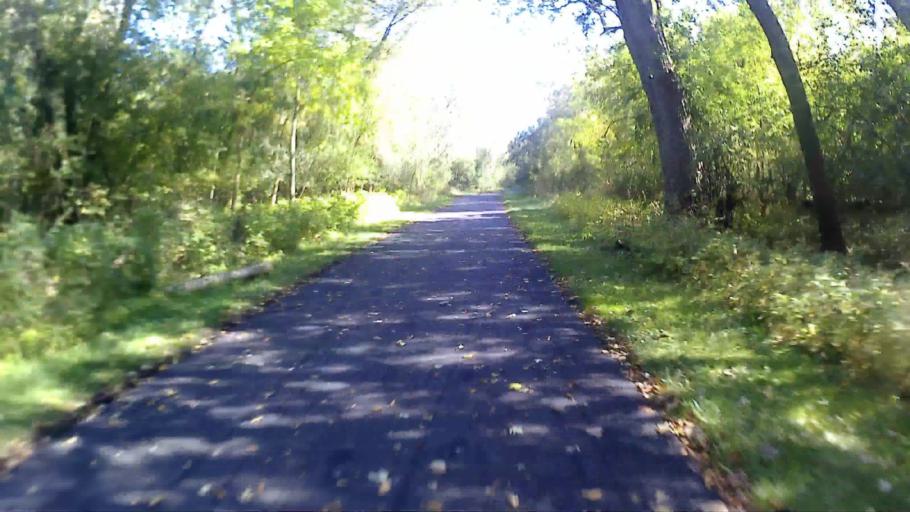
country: US
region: Illinois
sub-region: DuPage County
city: Addison
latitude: 41.9272
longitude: -87.9758
